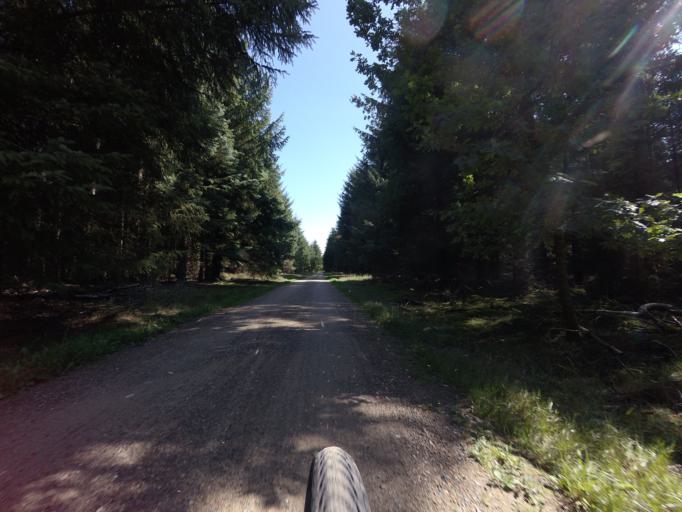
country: DK
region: North Denmark
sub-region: Hjorring Kommune
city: Hirtshals
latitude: 57.5835
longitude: 10.0627
